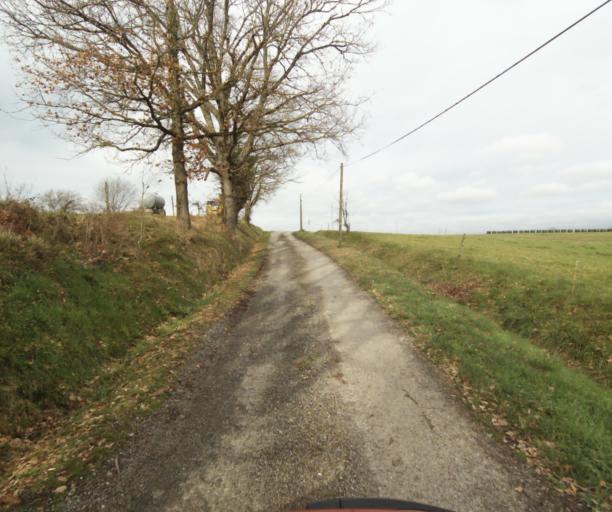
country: FR
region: Midi-Pyrenees
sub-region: Departement de l'Ariege
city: Verniolle
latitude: 43.0787
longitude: 1.7094
